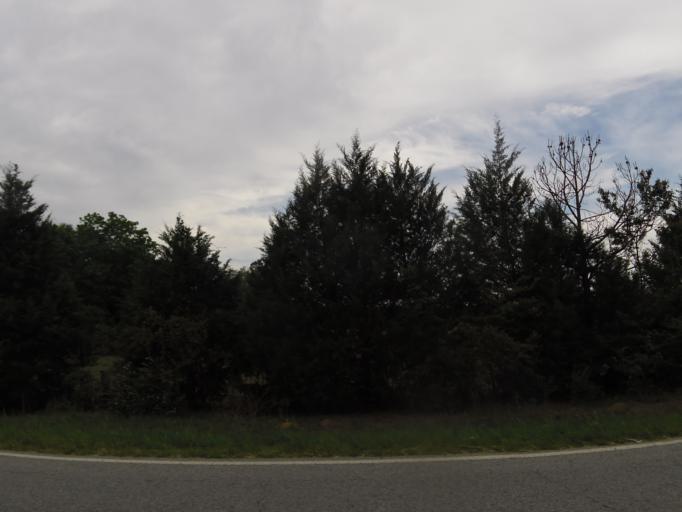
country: US
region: Georgia
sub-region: Emanuel County
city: Twin City
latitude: 32.4845
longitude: -82.2452
